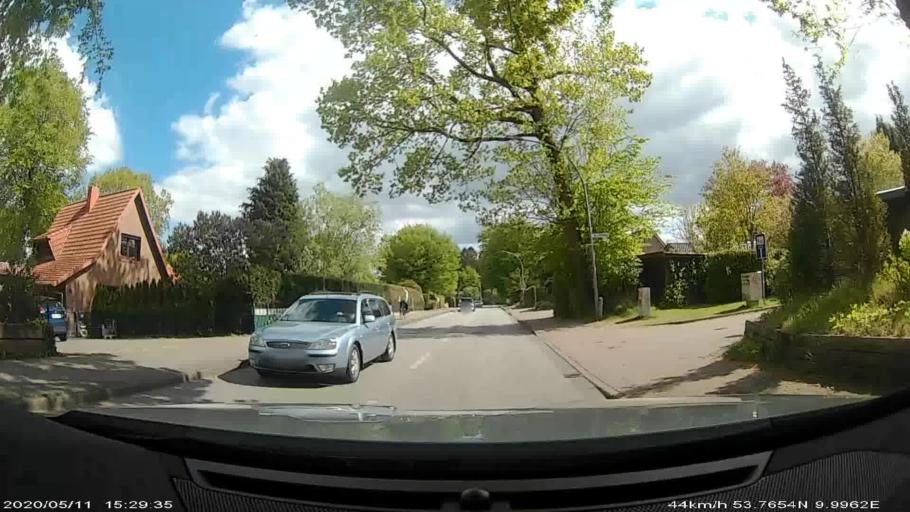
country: DE
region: Schleswig-Holstein
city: Henstedt-Ulzburg
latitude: 53.7564
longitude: 9.9966
